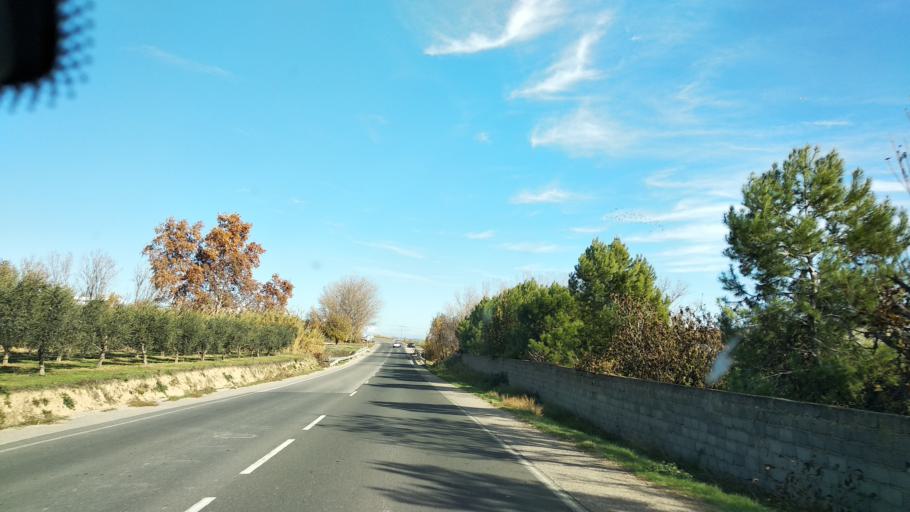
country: ES
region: Catalonia
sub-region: Provincia de Lleida
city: Termens
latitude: 41.7378
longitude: 0.7510
